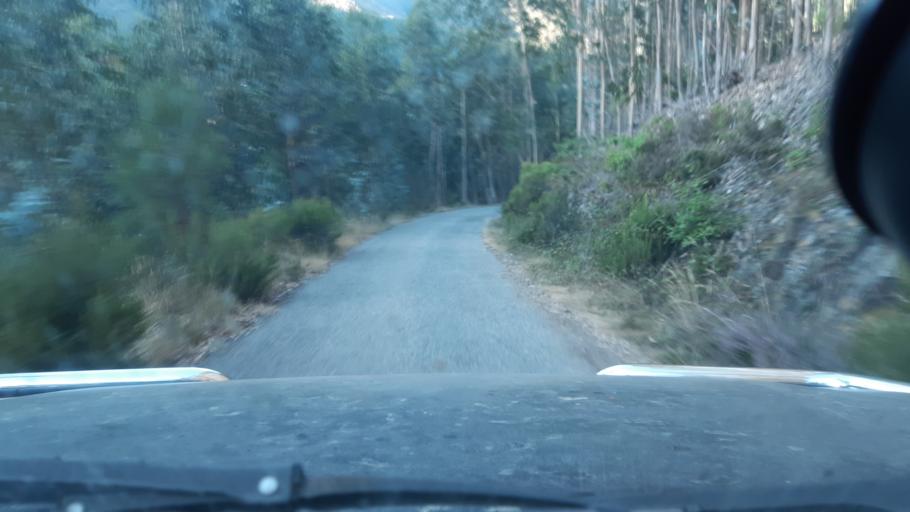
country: PT
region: Viseu
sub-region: Mortagua
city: Mortagua
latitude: 40.5274
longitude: -8.2561
